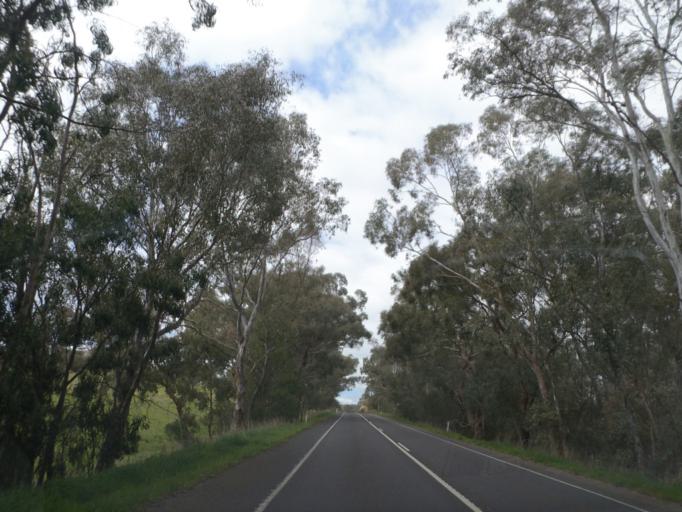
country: AU
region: Victoria
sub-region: Murrindindi
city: Kinglake West
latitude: -37.1313
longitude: 145.2283
